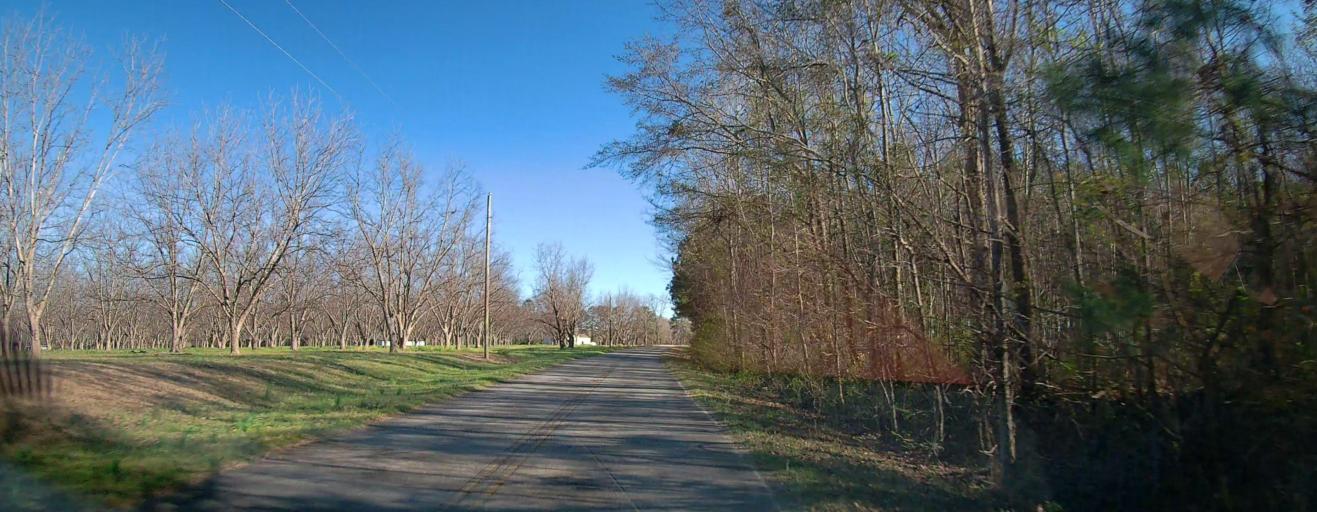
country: US
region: Georgia
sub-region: Peach County
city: Fort Valley
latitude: 32.6353
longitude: -83.8559
